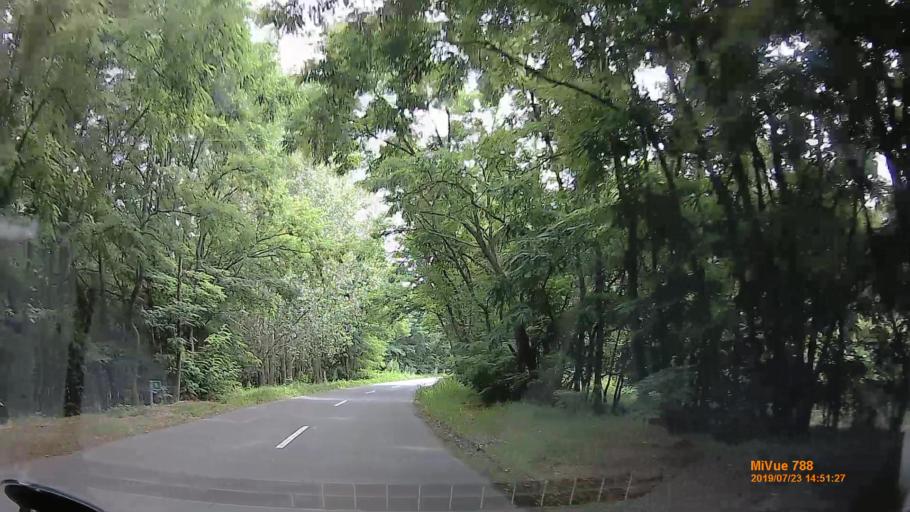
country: HU
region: Szabolcs-Szatmar-Bereg
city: Kalmanhaza
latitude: 47.8827
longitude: 21.6526
